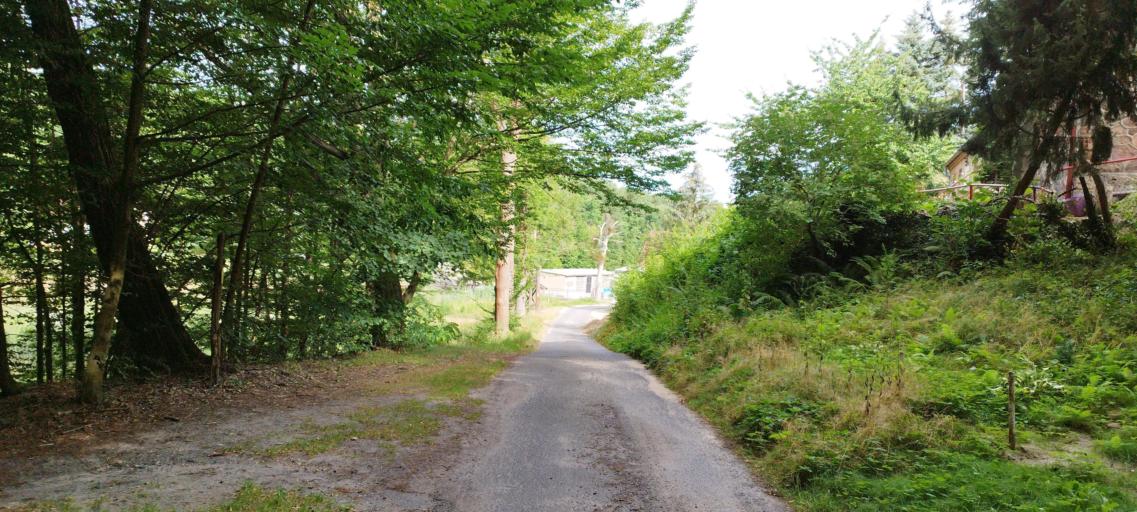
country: DE
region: Brandenburg
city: Mixdorf
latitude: 52.1062
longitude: 14.4782
